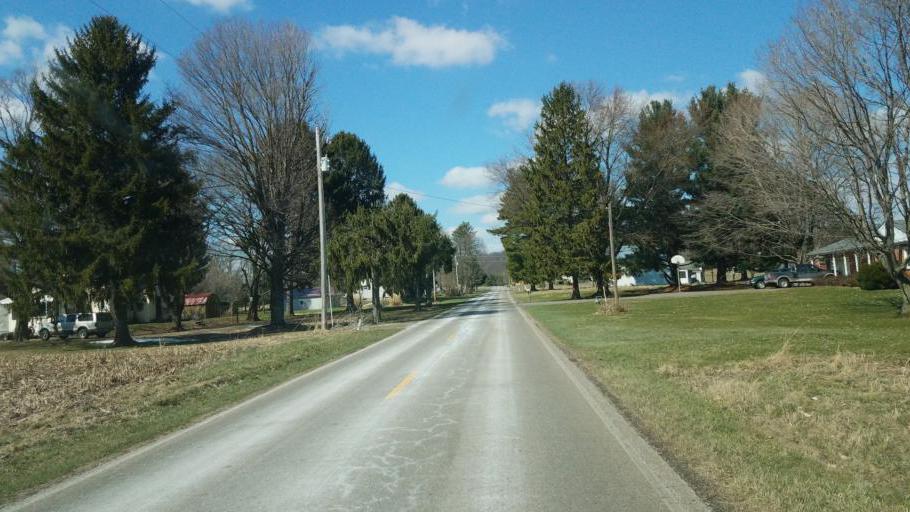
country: US
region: Ohio
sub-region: Knox County
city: Fredericktown
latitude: 40.4439
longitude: -82.5104
